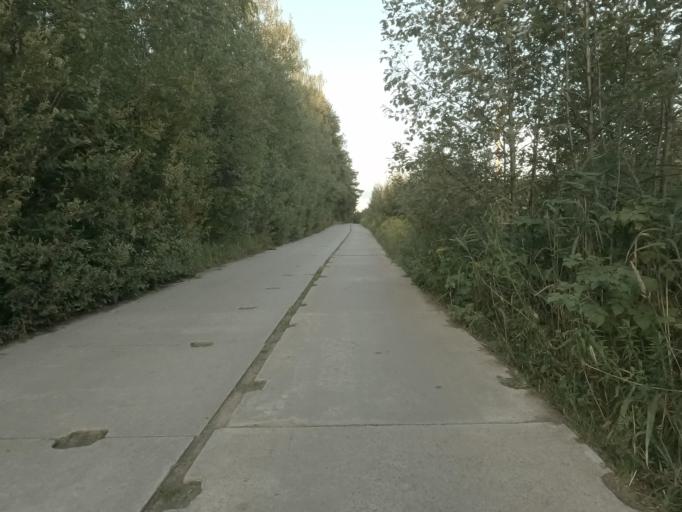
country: RU
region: Leningrad
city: Mga
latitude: 59.7611
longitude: 31.0103
